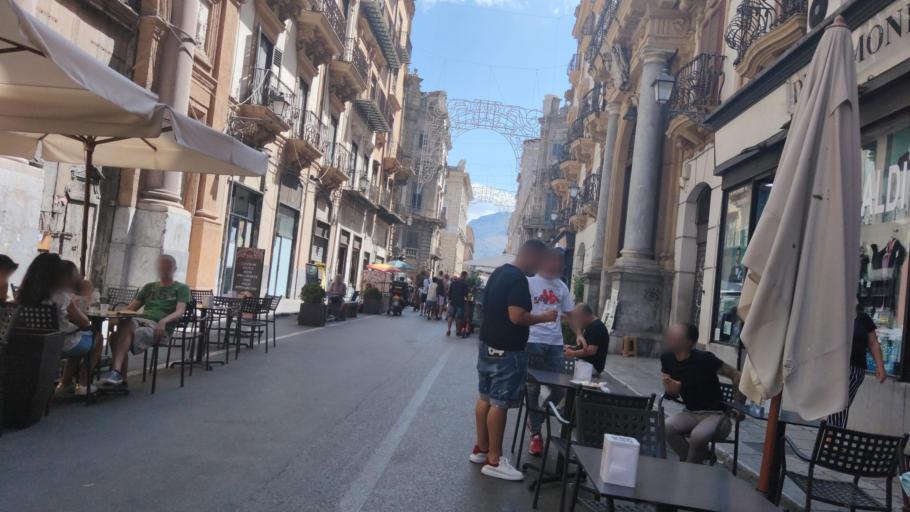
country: IT
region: Sicily
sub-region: Palermo
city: Palermo
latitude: 38.1162
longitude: 13.3611
